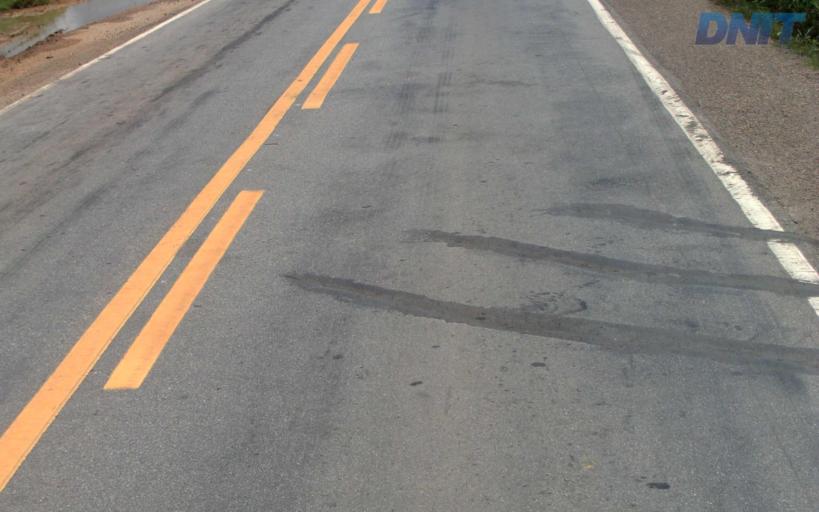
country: BR
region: Minas Gerais
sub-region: Belo Oriente
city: Belo Oriente
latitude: -19.1105
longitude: -42.2029
